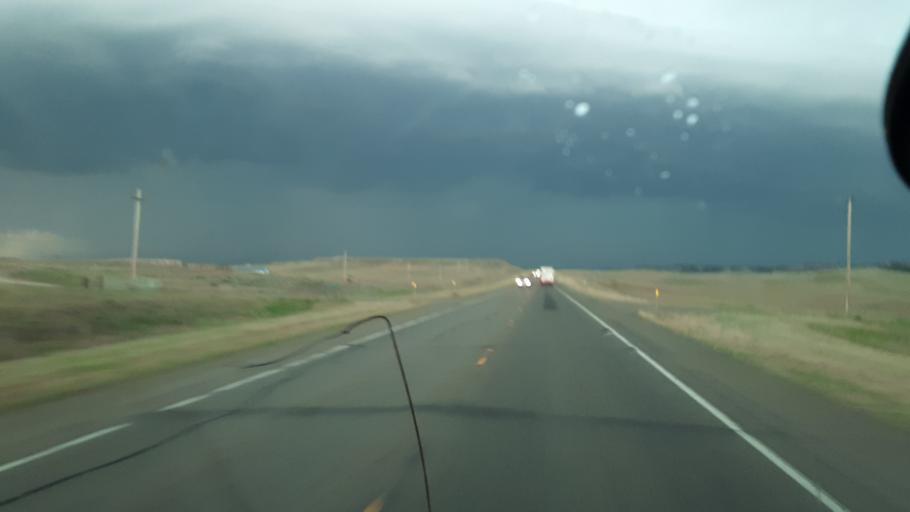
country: US
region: Montana
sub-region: Powder River County
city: Broadus
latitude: 45.4540
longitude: -105.4393
